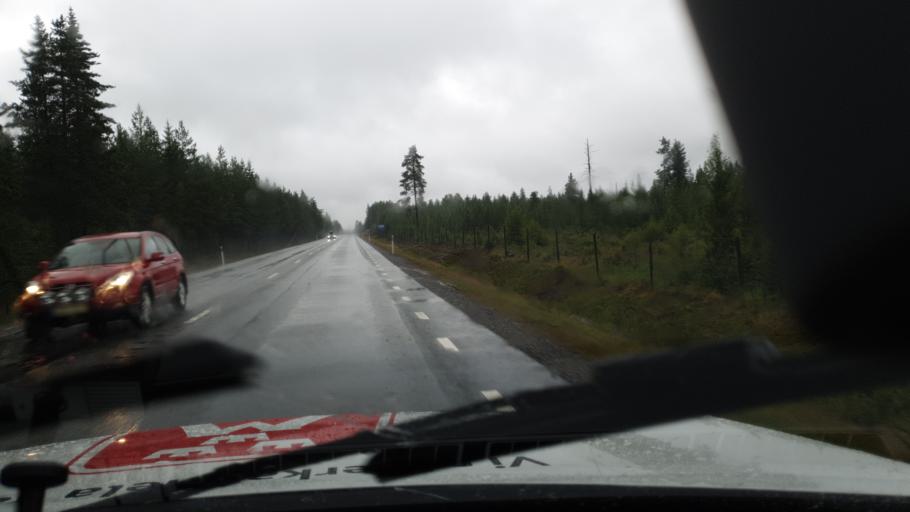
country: SE
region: Vaesterbotten
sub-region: Skelleftea Kommun
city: Burea
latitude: 64.5882
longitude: 21.2164
